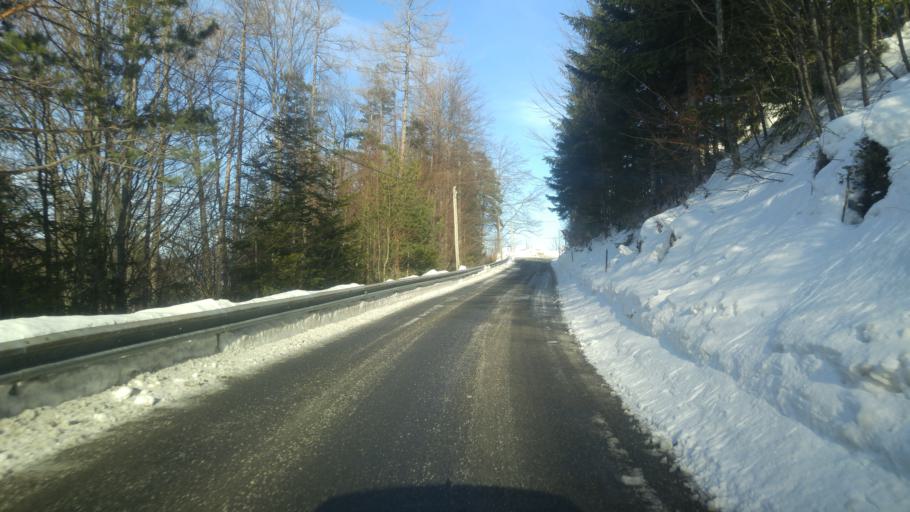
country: AT
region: Lower Austria
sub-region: Politischer Bezirk Lilienfeld
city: Hohenberg
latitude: 47.8796
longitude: 15.6214
